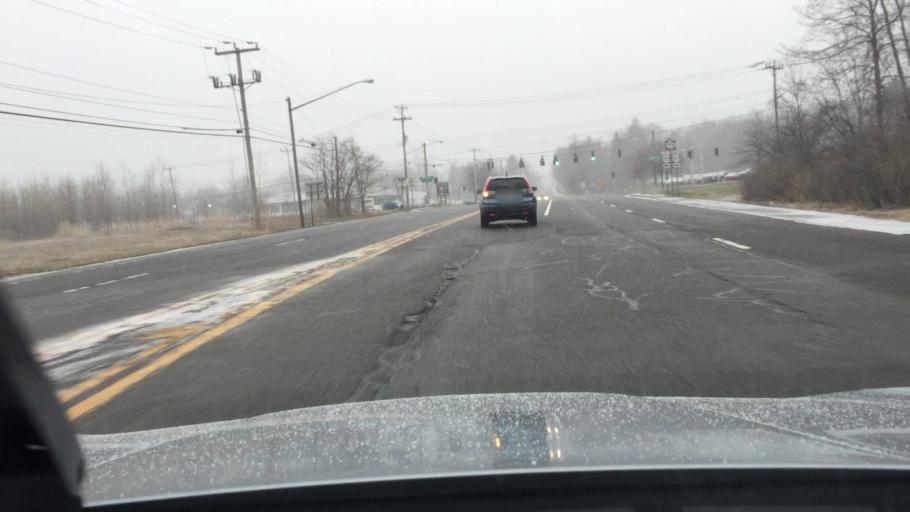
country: US
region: New York
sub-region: Erie County
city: Orchard Park
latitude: 42.7891
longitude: -78.7619
